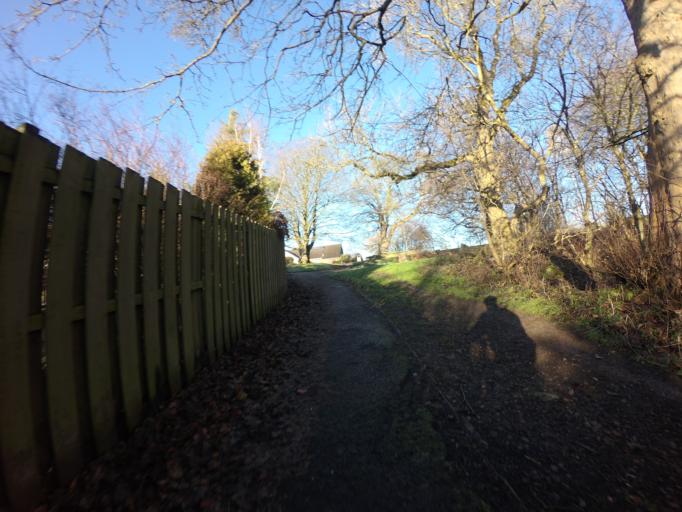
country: GB
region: Scotland
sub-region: West Lothian
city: Livingston
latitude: 55.8873
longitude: -3.5286
